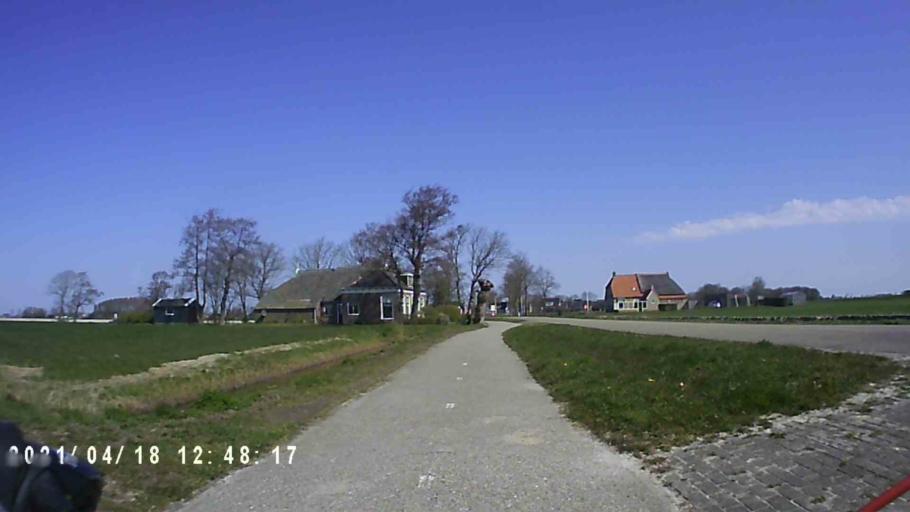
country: NL
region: Friesland
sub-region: Gemeente Dongeradeel
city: Dokkum
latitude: 53.3728
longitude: 6.0511
